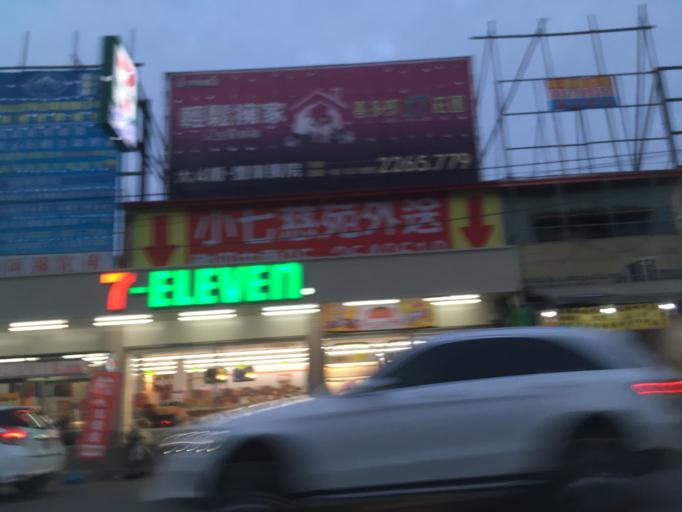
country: TW
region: Taiwan
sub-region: Chiayi
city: Jiayi Shi
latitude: 23.5970
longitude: 120.4575
